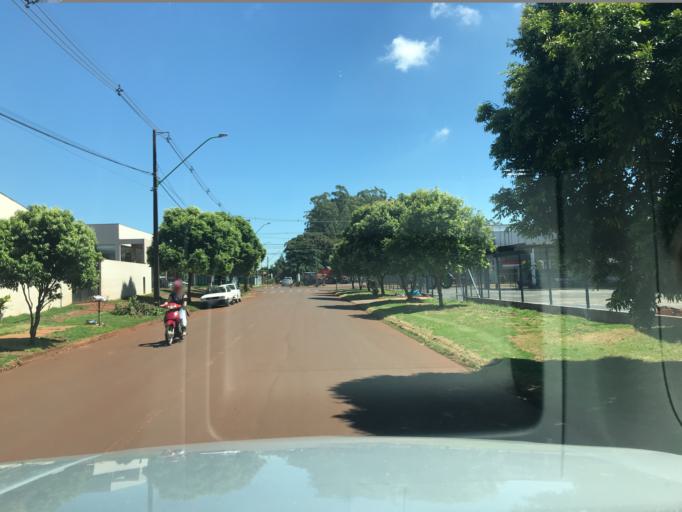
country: BR
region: Parana
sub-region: Palotina
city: Palotina
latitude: -24.2825
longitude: -53.8341
